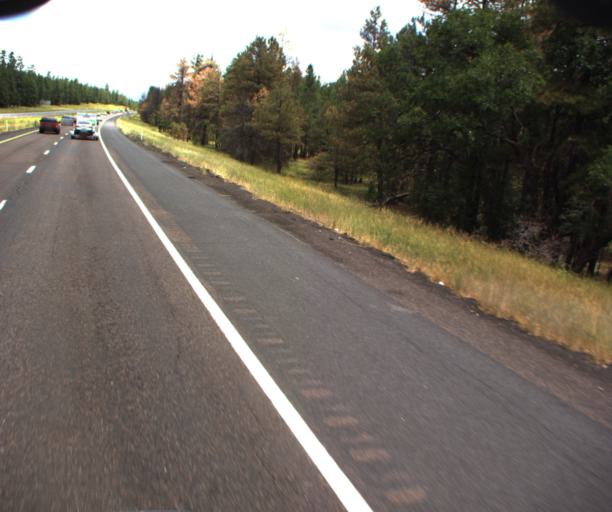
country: US
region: Arizona
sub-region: Coconino County
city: Mountainaire
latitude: 34.9889
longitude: -111.6867
